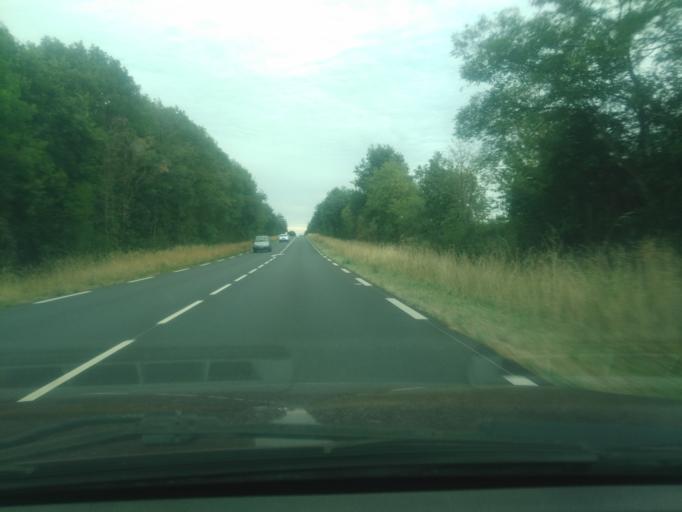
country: FR
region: Centre
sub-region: Departement de l'Indre
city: Le Pechereau
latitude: 46.6008
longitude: 1.6119
